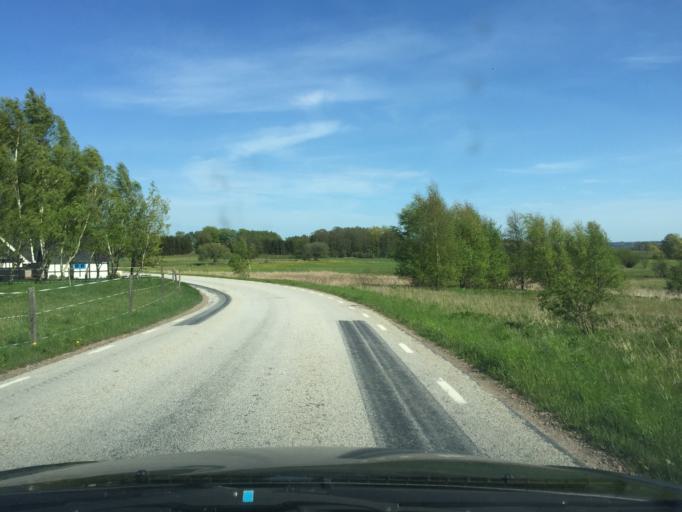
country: SE
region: Skane
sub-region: Sjobo Kommun
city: Blentarp
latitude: 55.5734
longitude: 13.5772
